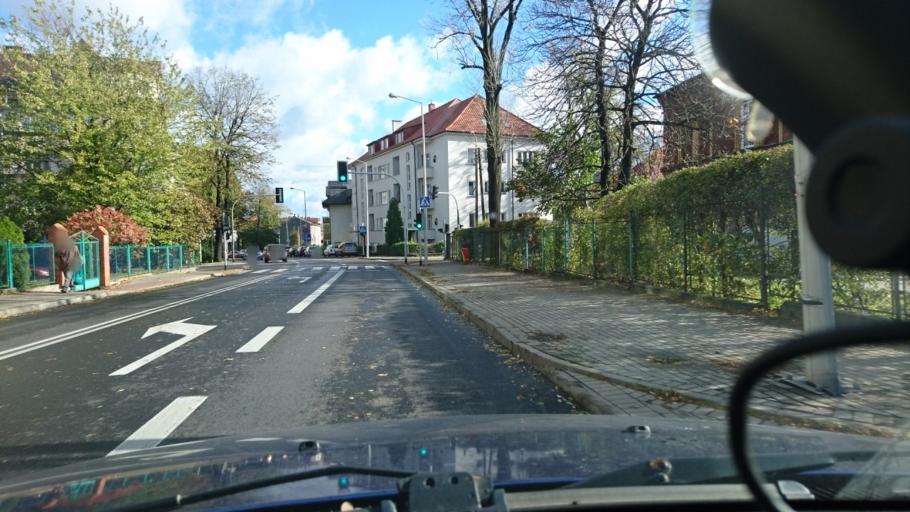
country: PL
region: Silesian Voivodeship
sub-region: Bielsko-Biala
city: Bielsko-Biala
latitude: 49.8235
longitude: 19.0350
